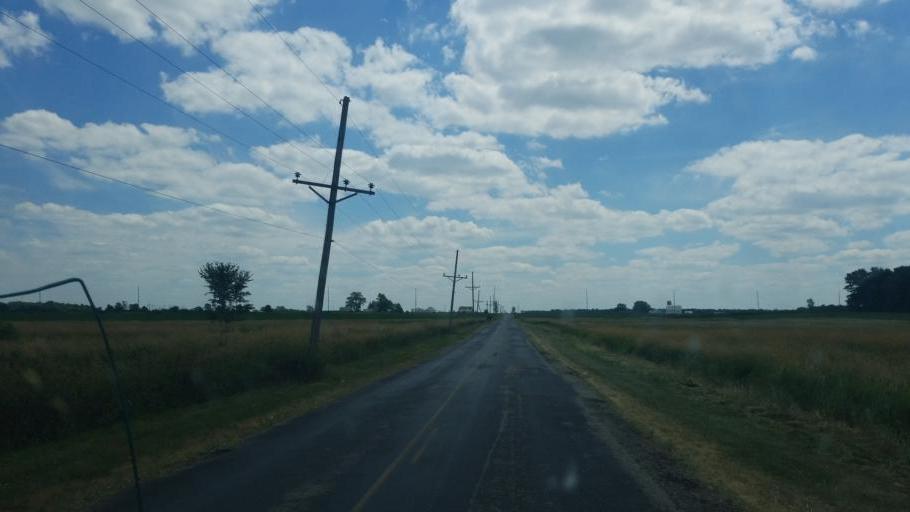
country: US
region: Ohio
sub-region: Williams County
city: Edgerton
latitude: 41.4623
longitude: -84.6912
